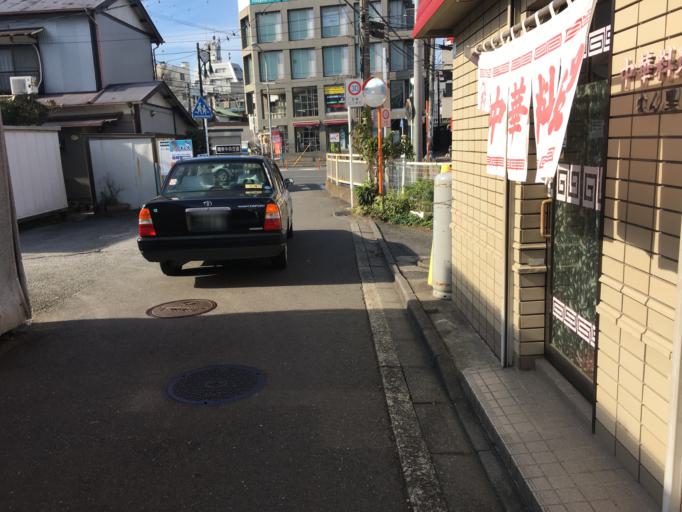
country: JP
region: Tokyo
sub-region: Machida-shi
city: Machida
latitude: 35.5137
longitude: 139.5424
